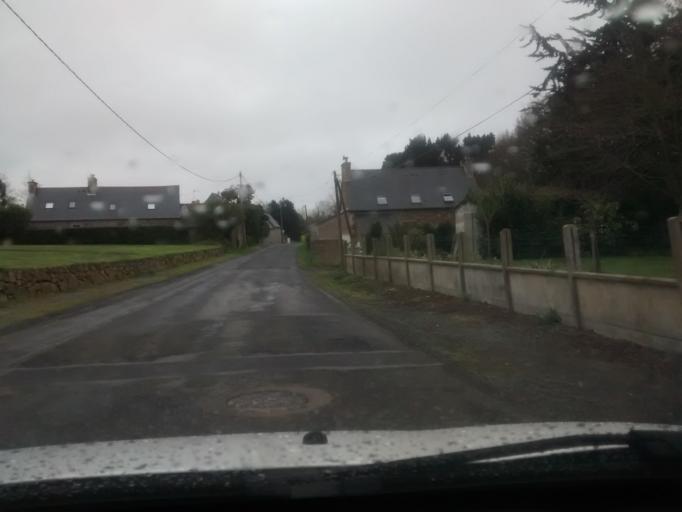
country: FR
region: Brittany
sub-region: Departement des Cotes-d'Armor
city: Penvenan
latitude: 48.8248
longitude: -3.2828
